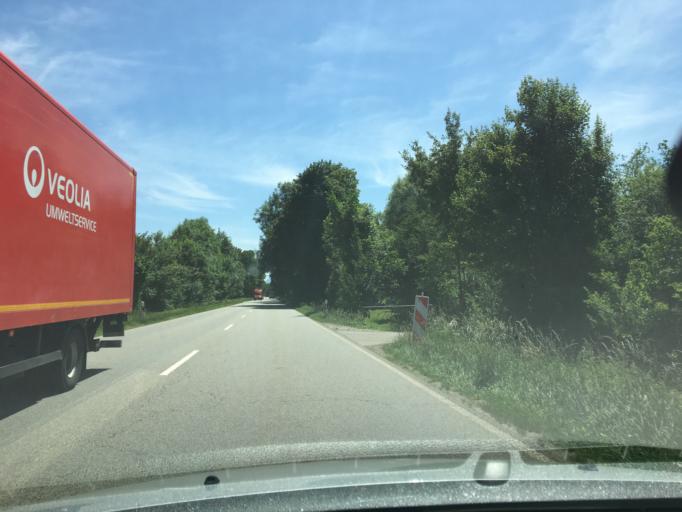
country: DE
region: Bavaria
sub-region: Upper Bavaria
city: Freilassing
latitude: 47.8648
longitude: 12.9790
